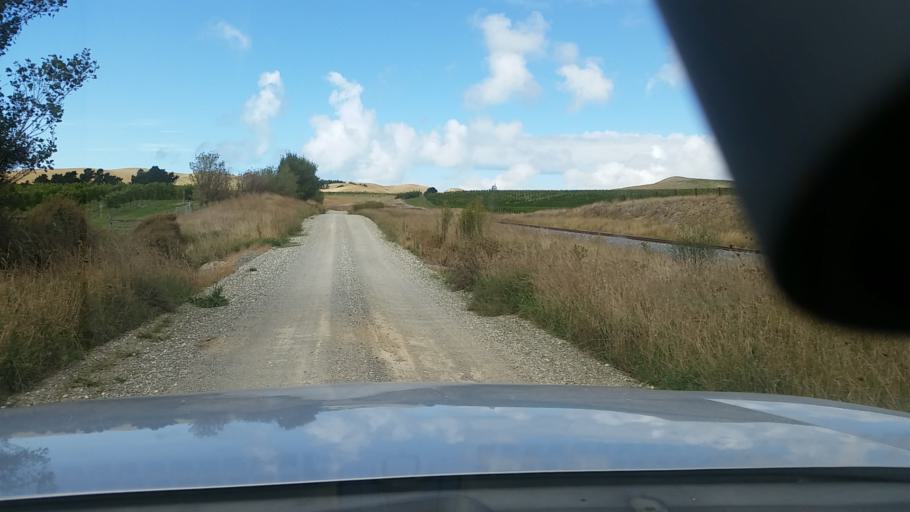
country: NZ
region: Marlborough
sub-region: Marlborough District
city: Blenheim
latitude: -41.6874
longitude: 174.1338
